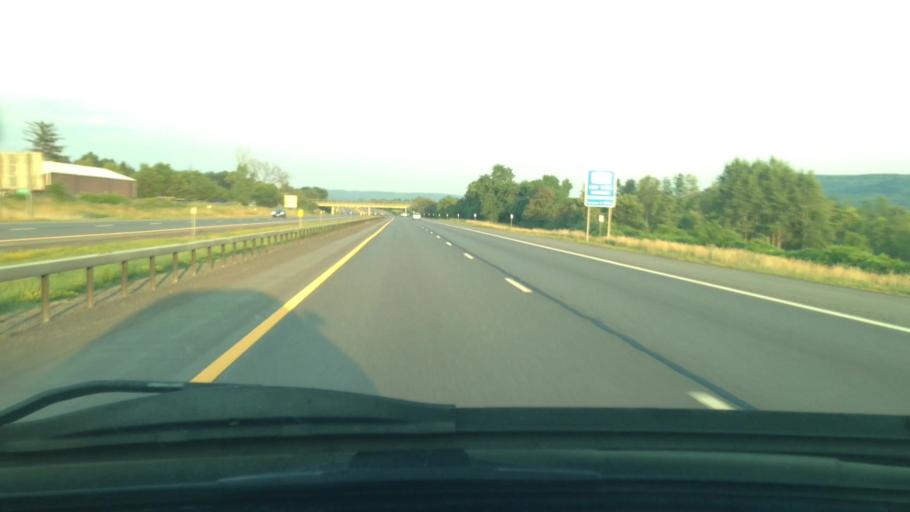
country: US
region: New York
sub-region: Oneida County
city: Utica
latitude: 43.0999
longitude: -75.1581
